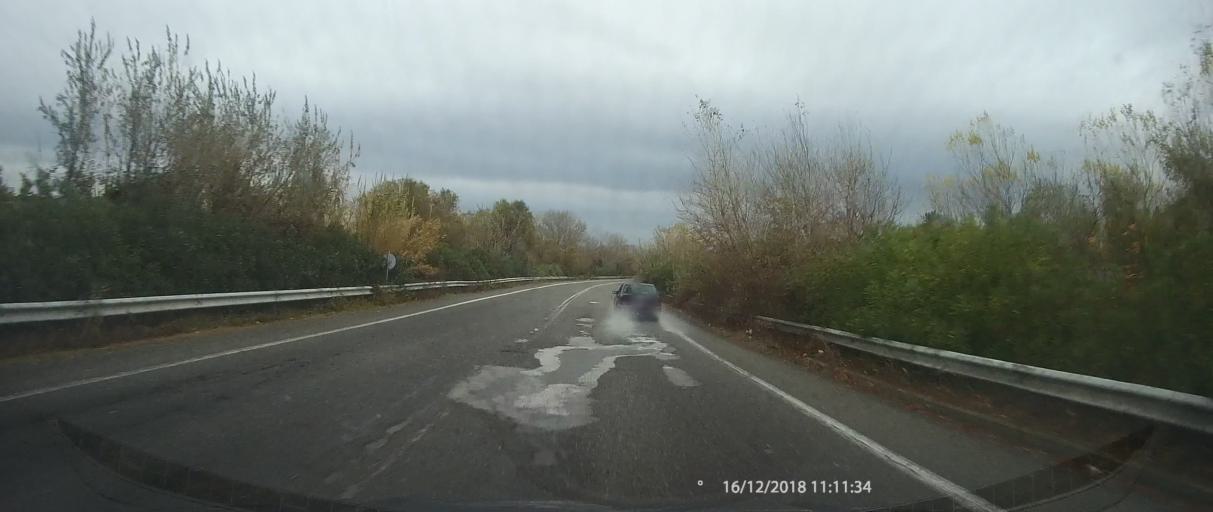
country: GR
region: East Macedonia and Thrace
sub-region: Nomos Xanthis
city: Petrochori
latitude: 41.0837
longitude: 24.7634
